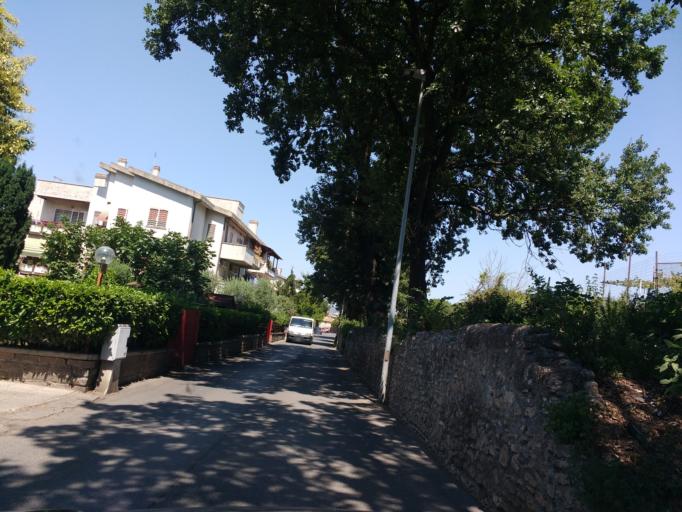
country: IT
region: Latium
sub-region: Citta metropolitana di Roma Capitale
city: Villa Adriana
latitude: 41.9507
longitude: 12.7786
